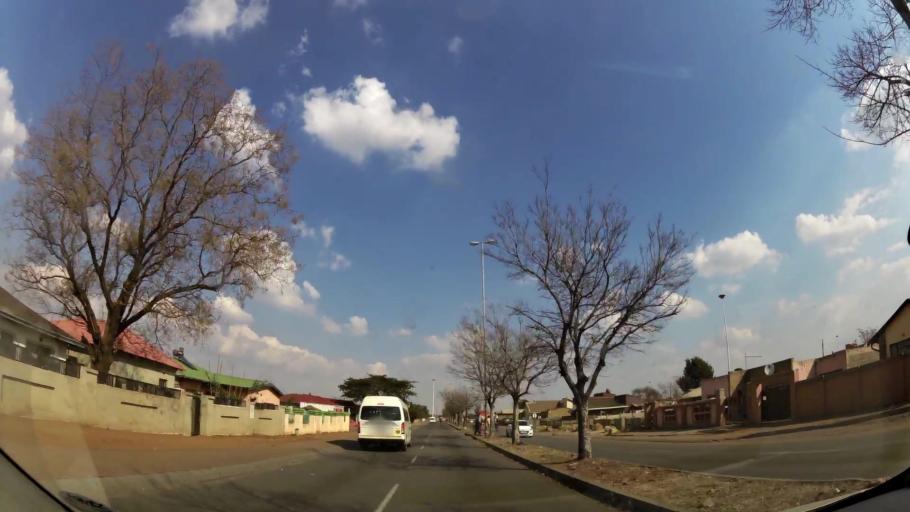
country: ZA
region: Gauteng
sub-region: Ekurhuleni Metropolitan Municipality
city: Germiston
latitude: -26.3201
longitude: 28.1573
